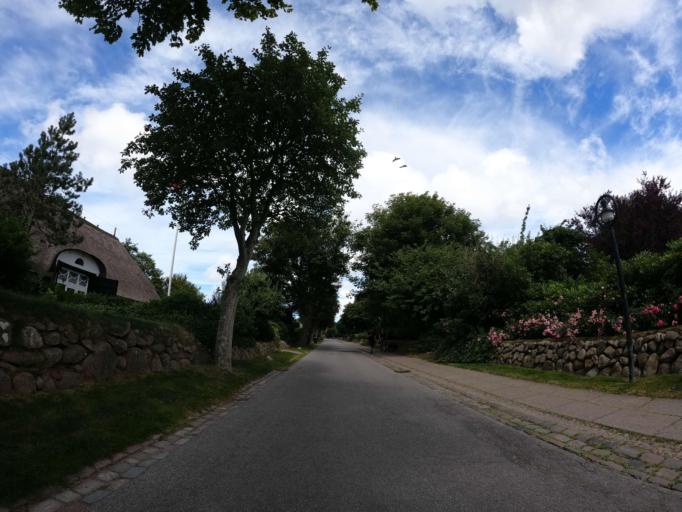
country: DE
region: Schleswig-Holstein
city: Keitum
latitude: 54.8903
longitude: 8.3705
